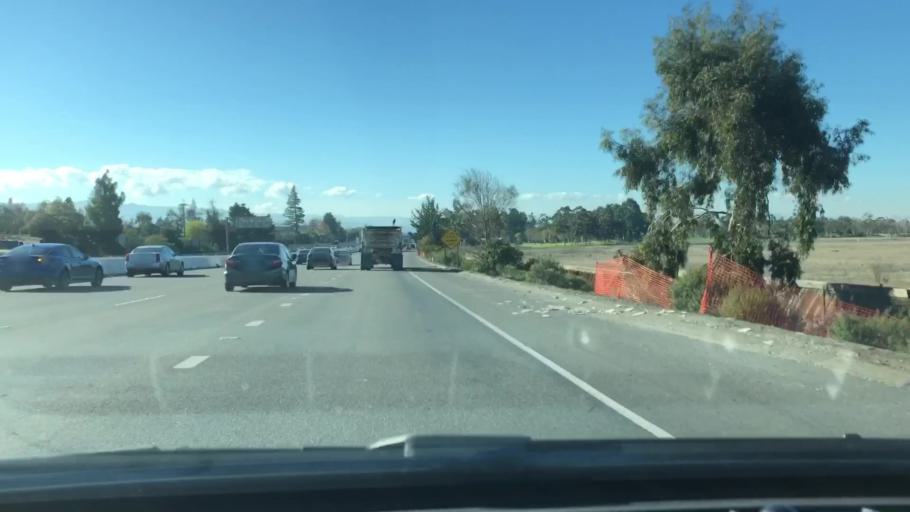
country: US
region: California
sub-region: Santa Clara County
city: Sunnyvale
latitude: 37.4121
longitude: -121.9880
